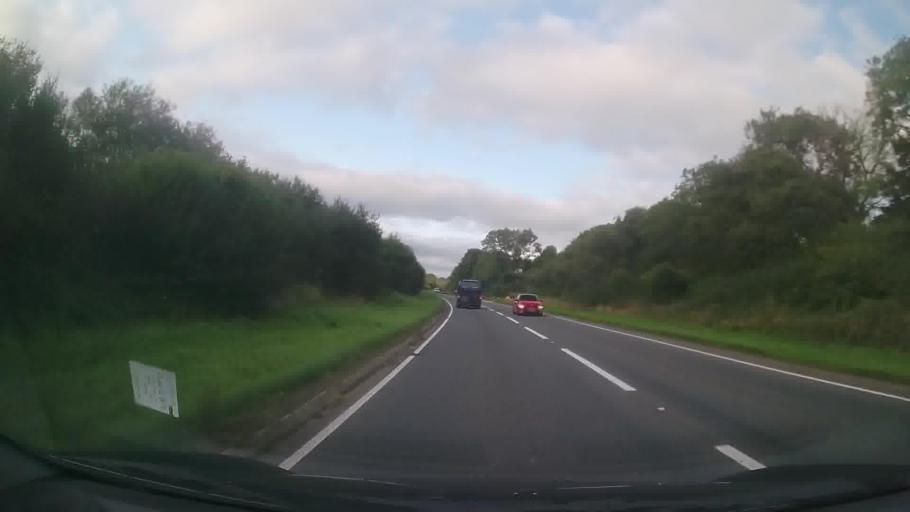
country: GB
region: Wales
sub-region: Pembrokeshire
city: Jeffreyston
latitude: 51.7093
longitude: -4.7643
